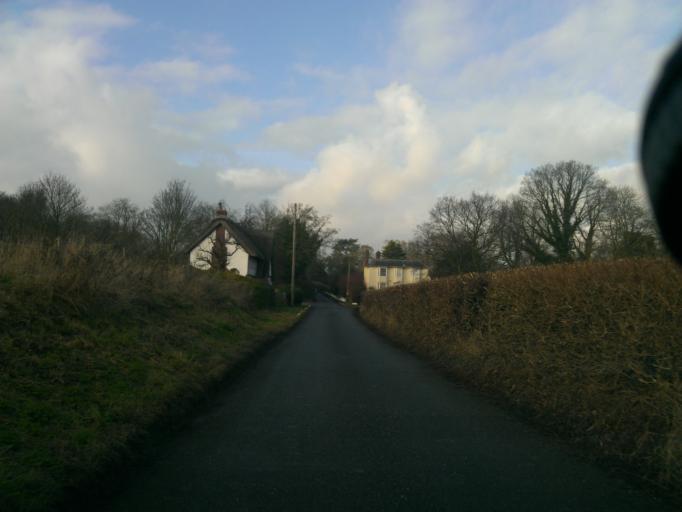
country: GB
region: England
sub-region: Suffolk
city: Sudbury
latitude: 51.9953
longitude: 0.7486
